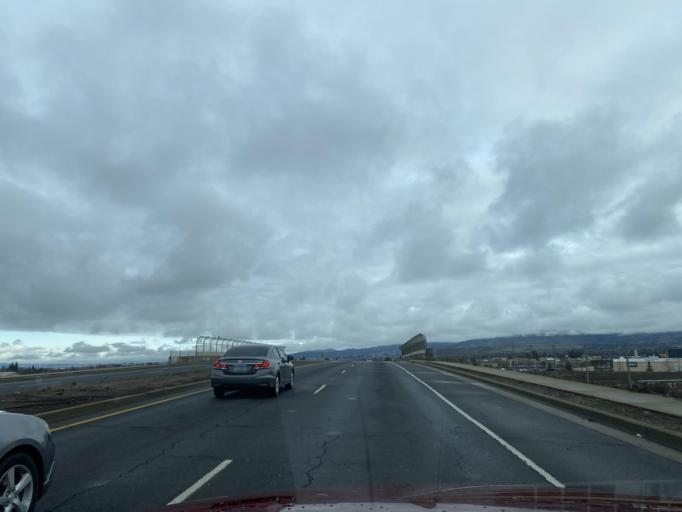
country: US
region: Oregon
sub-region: Jackson County
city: Medford
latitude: 42.3420
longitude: -122.8900
